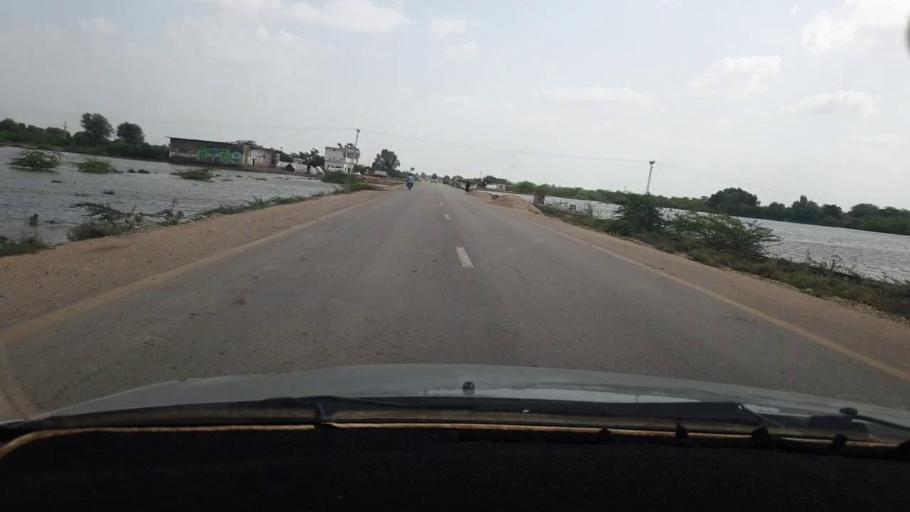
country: PK
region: Sindh
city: Naukot
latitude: 24.9892
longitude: 69.2920
